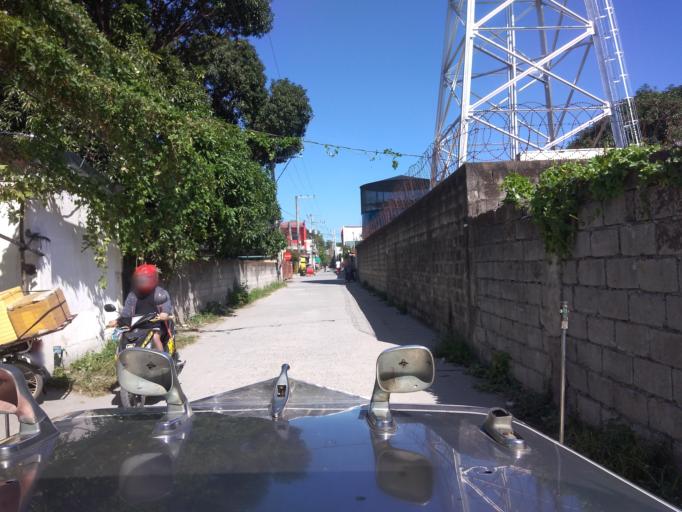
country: PH
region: Central Luzon
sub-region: Province of Pampanga
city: Calibutbut
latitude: 15.1101
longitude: 120.6048
